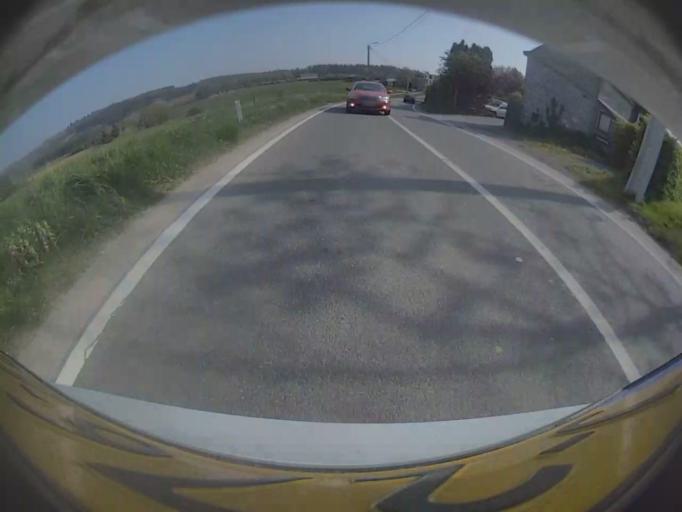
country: BE
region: Wallonia
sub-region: Province de Namur
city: Somme-Leuze
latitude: 50.3450
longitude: 5.2957
